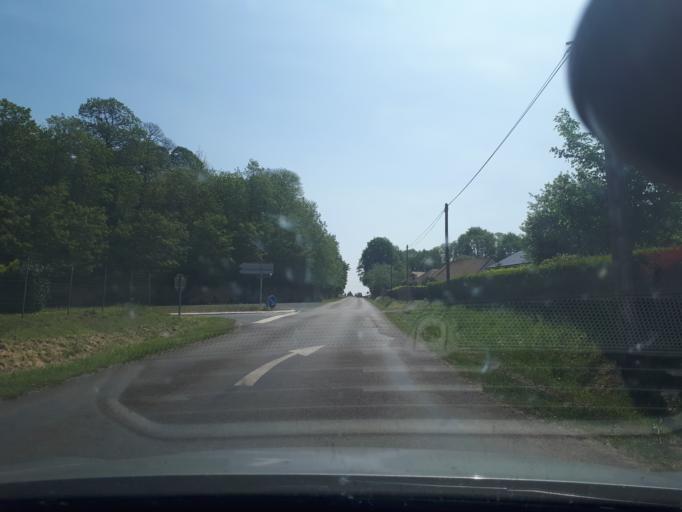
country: FR
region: Pays de la Loire
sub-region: Departement de la Sarthe
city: Montfort-le-Gesnois
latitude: 48.0523
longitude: 0.3924
